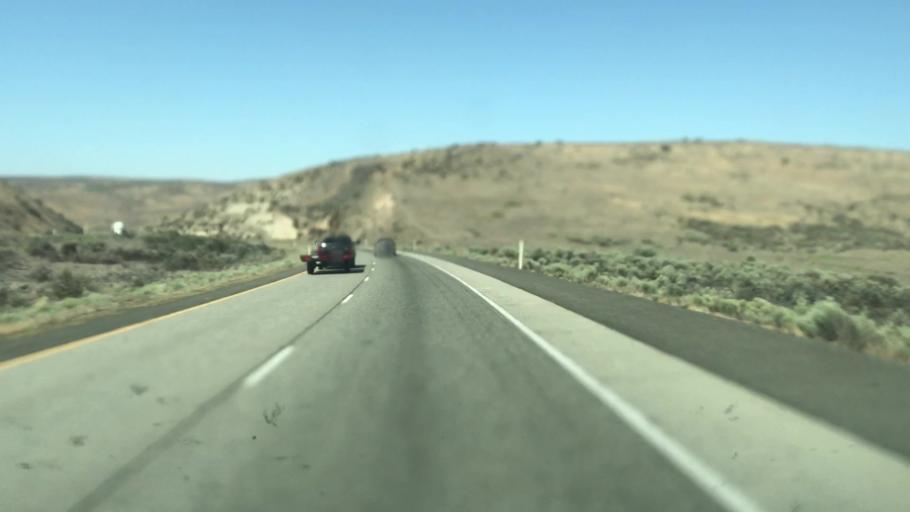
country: US
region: Washington
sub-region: Yakima County
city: Terrace Heights
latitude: 46.7286
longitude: -120.3873
